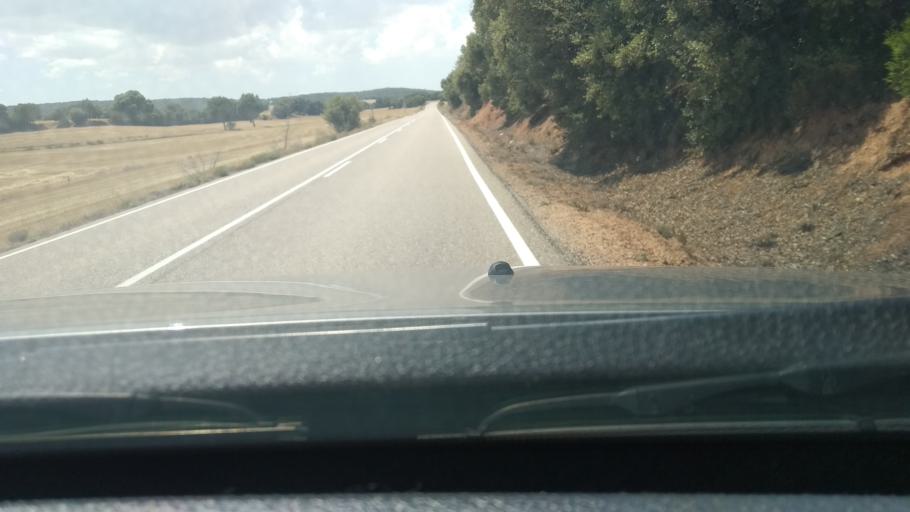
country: ES
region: Castille and Leon
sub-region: Provincia de Burgos
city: Quintanilla de la Mata
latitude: 41.9846
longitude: -3.7815
